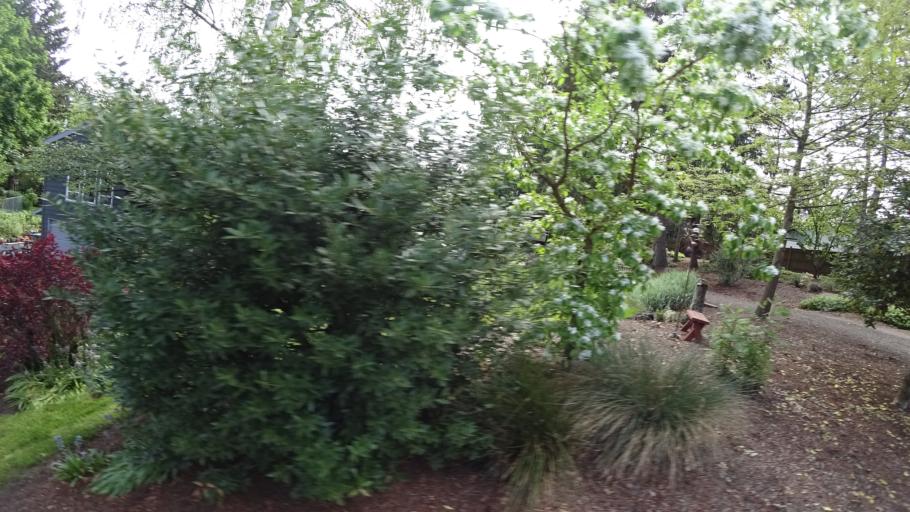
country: US
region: Oregon
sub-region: Washington County
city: Beaverton
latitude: 45.4653
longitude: -122.8138
